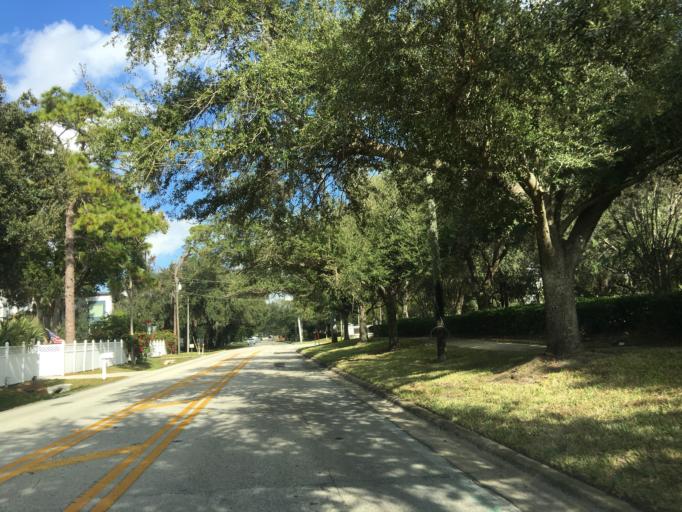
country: US
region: Florida
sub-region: Orange County
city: Eatonville
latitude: 28.6207
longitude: -81.3982
